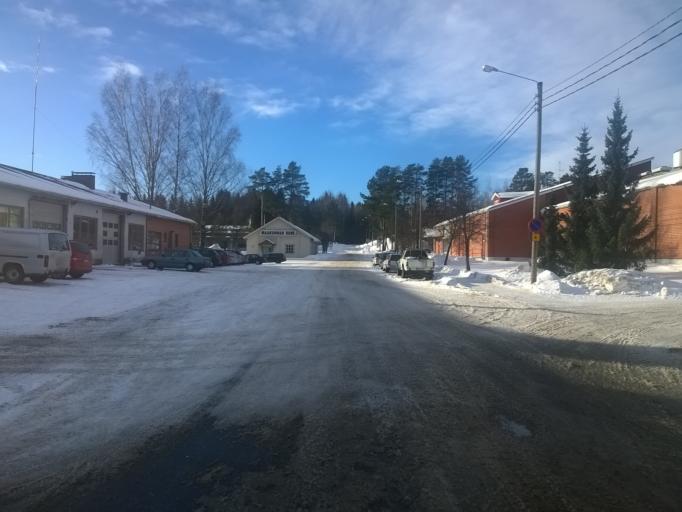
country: FI
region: Southern Savonia
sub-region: Mikkeli
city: Mikkeli
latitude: 61.6810
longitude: 27.2510
